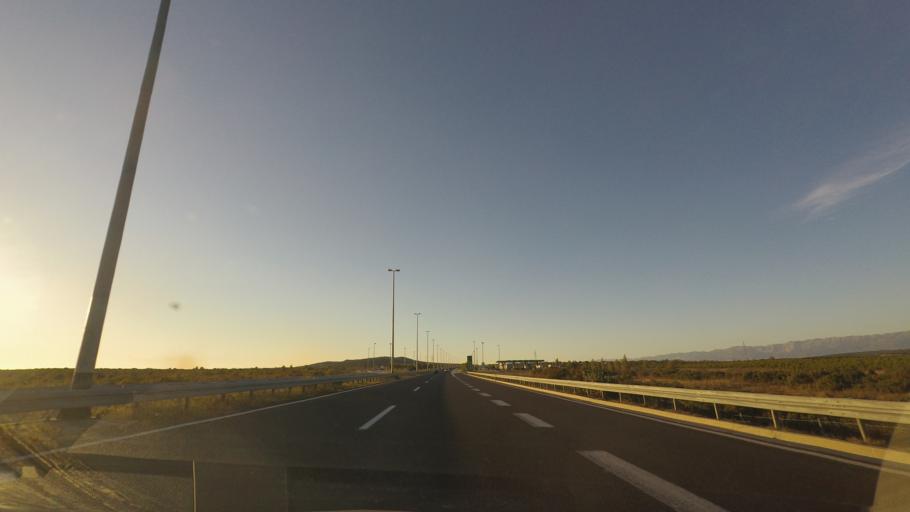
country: HR
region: Zadarska
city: Polaca
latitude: 44.0596
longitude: 15.5346
